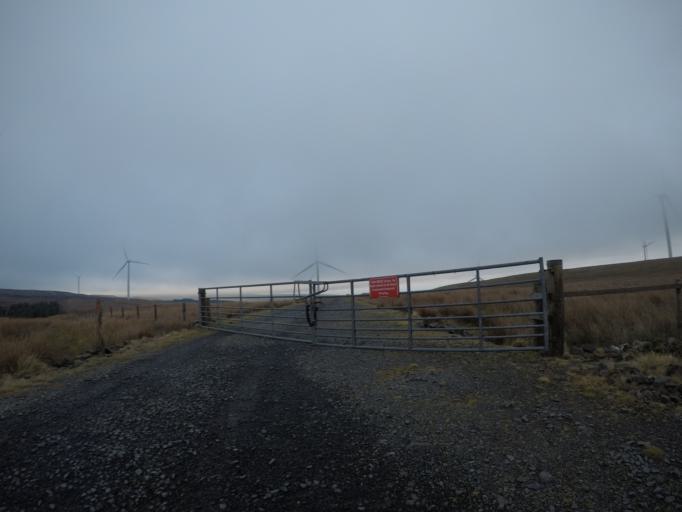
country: GB
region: Scotland
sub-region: North Ayrshire
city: Dalry
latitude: 55.7374
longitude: -4.7824
